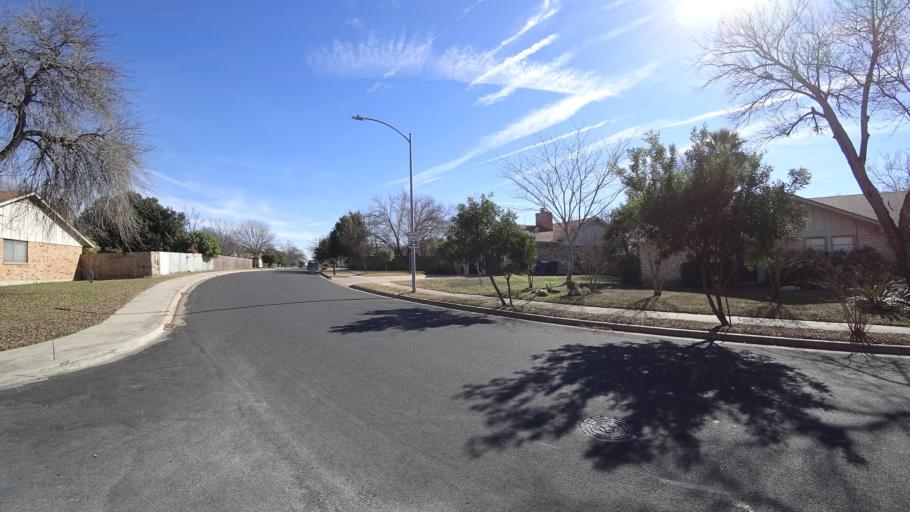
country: US
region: Texas
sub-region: Travis County
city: Wells Branch
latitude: 30.3774
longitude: -97.6994
